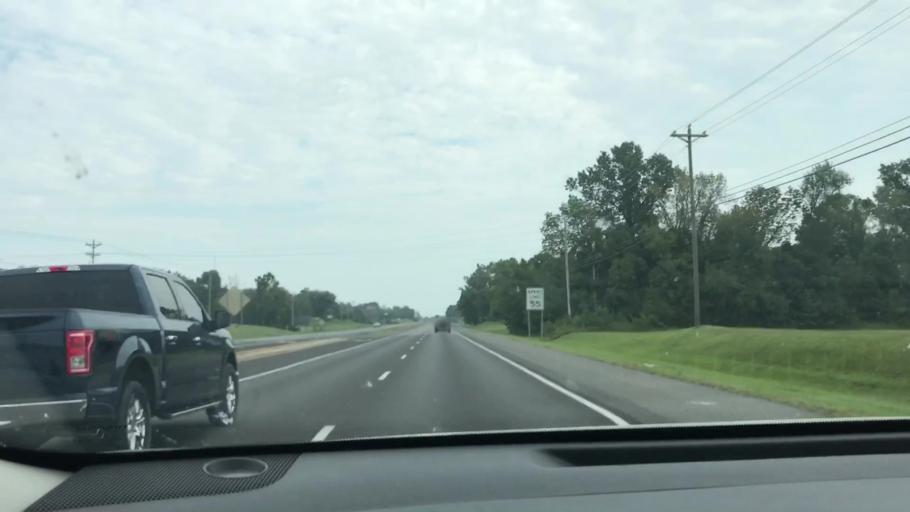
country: US
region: Kentucky
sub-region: Calloway County
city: Murray
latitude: 36.6602
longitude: -88.3056
